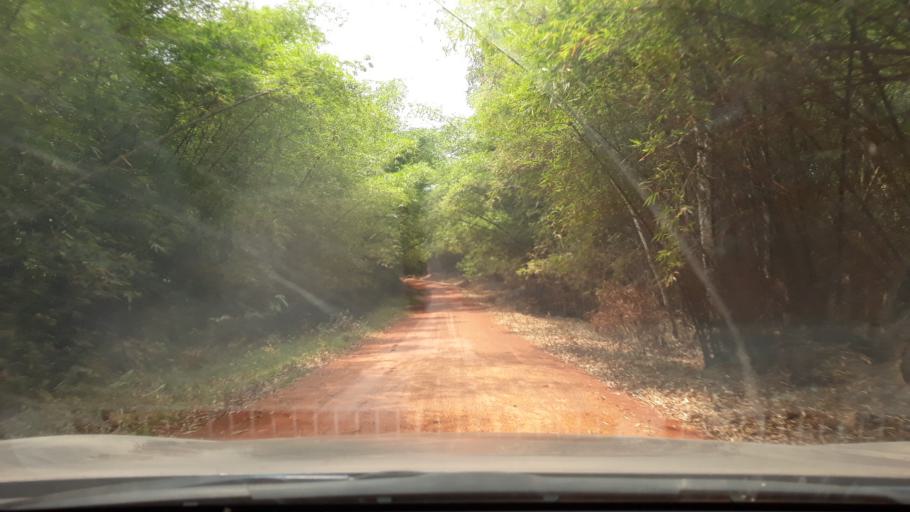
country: CD
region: Eastern Province
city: Buta
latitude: 2.3012
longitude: 25.0274
